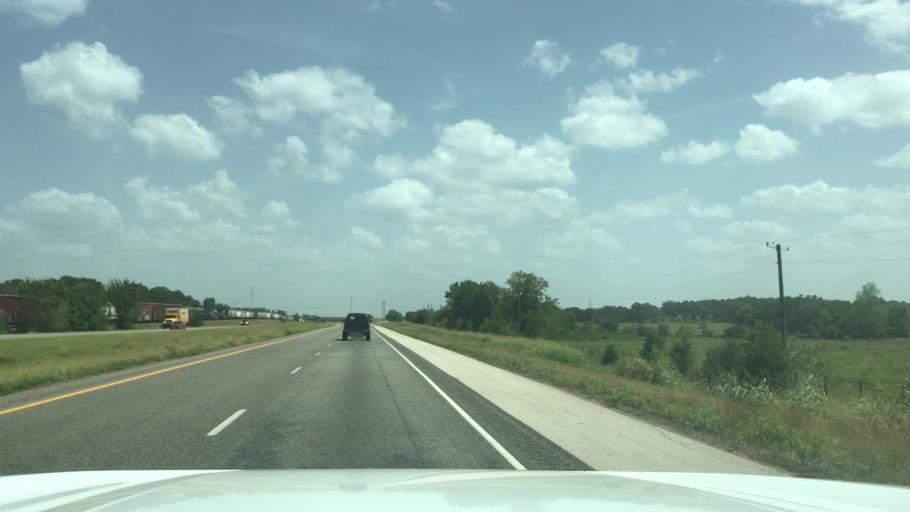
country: US
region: Texas
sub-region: Robertson County
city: Hearne
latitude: 30.9141
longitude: -96.6167
